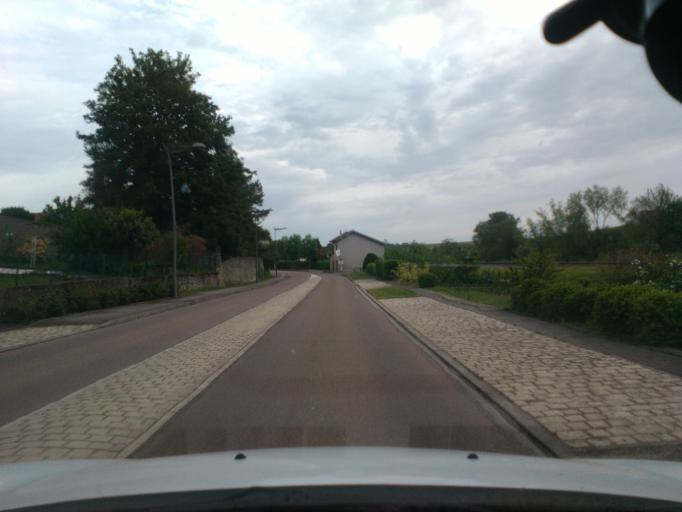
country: FR
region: Lorraine
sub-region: Departement des Vosges
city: Mirecourt
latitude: 48.3201
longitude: 6.1259
